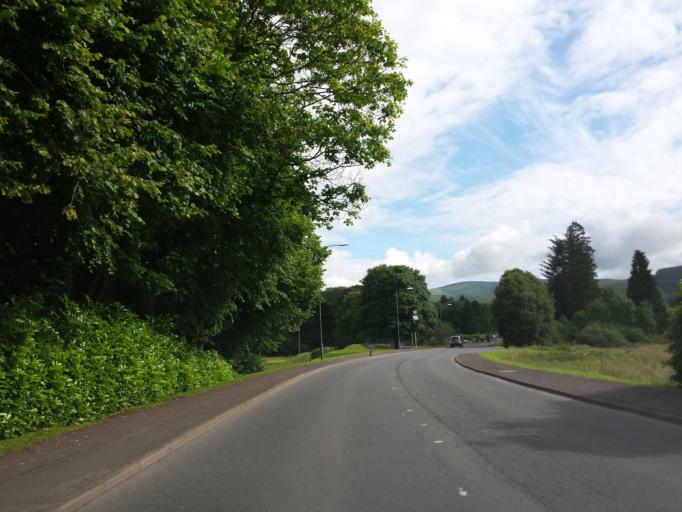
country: GB
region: Scotland
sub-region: Dumfries and Galloway
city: Moffat
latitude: 55.3279
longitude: -3.4471
